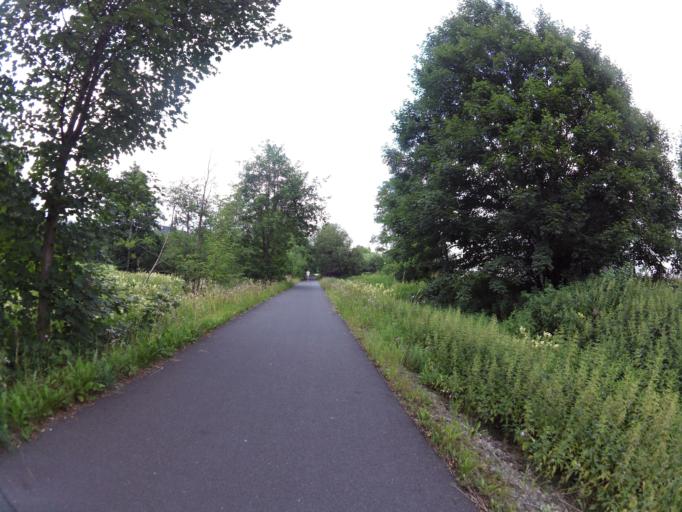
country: DE
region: Thuringia
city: Schleiz
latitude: 50.5792
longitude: 11.8029
